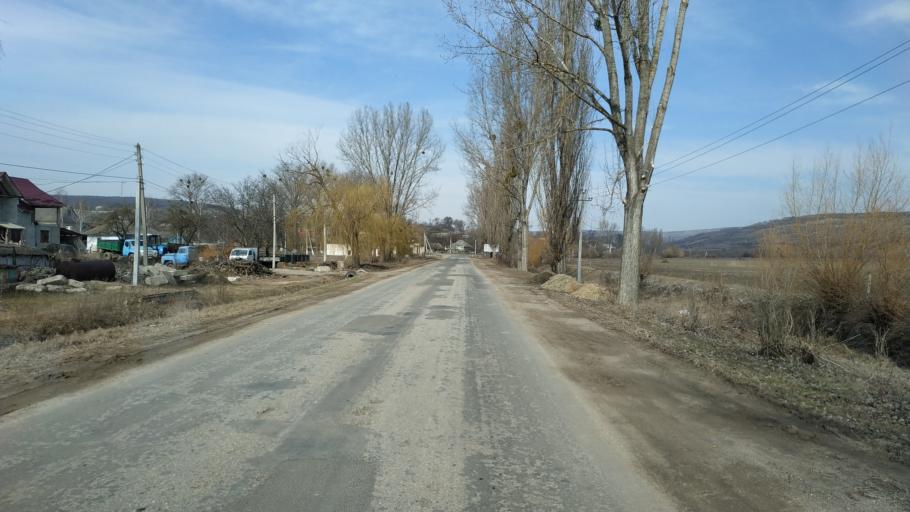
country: MD
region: Nisporeni
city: Nisporeni
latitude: 47.1474
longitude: 28.1091
